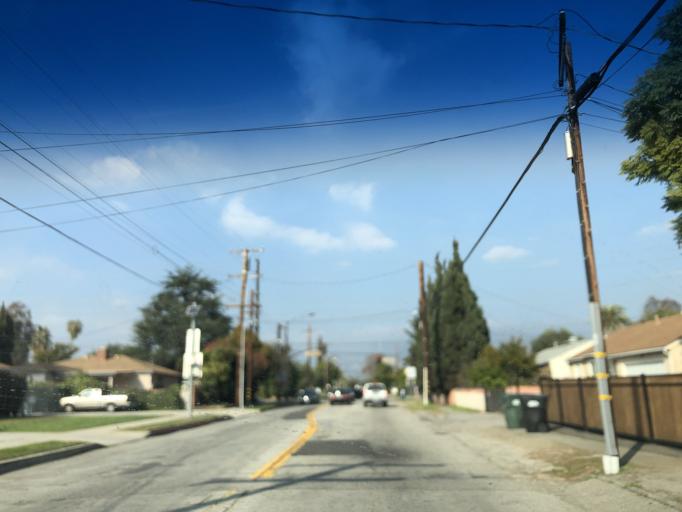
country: US
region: California
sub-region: Los Angeles County
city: East San Gabriel
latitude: 34.0983
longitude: -118.0837
